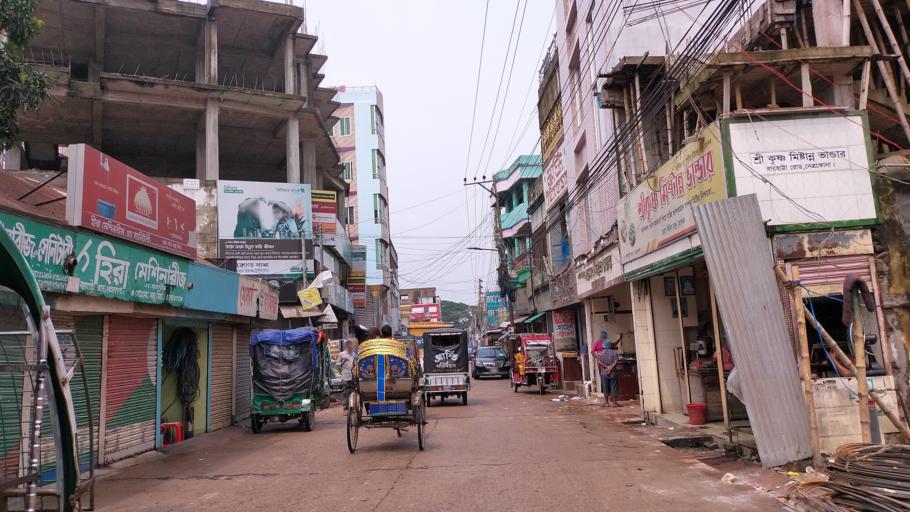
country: BD
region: Dhaka
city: Netrakona
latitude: 24.8853
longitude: 90.7345
